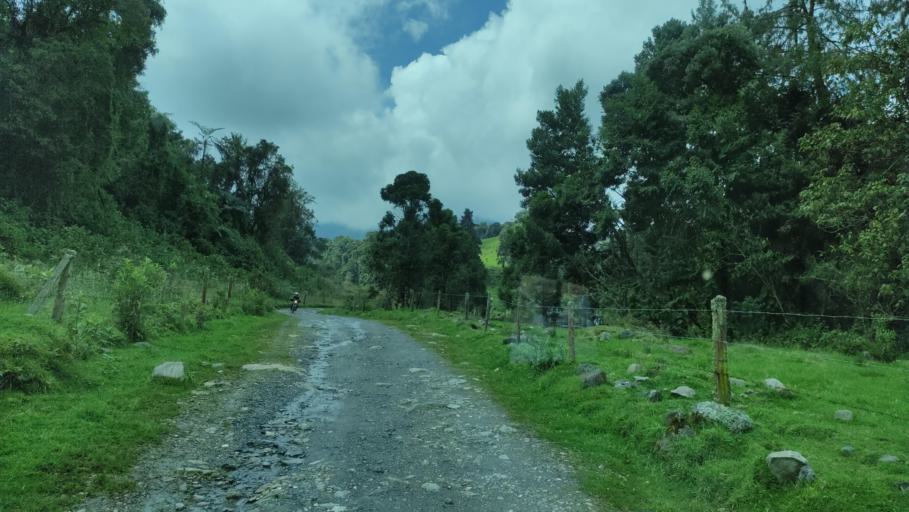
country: CO
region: Caldas
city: Villamaria
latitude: 4.9850
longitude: -75.4420
